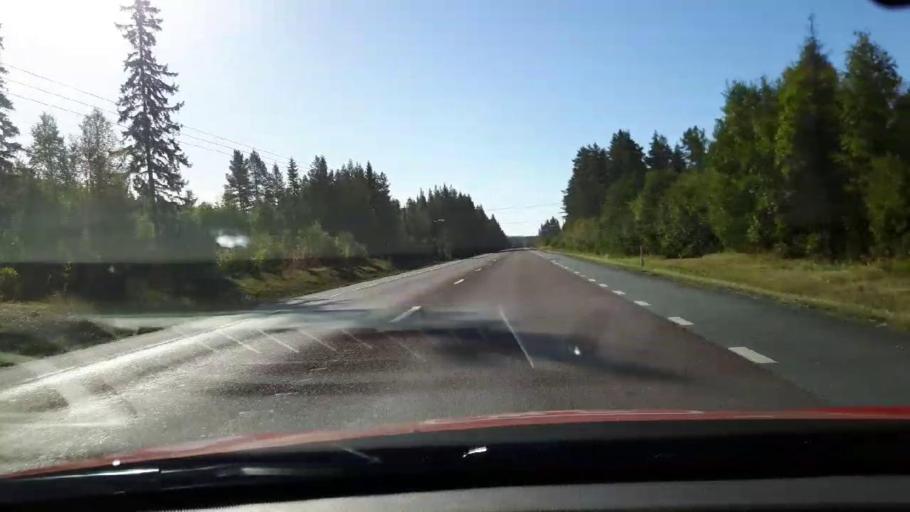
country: SE
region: Jaemtland
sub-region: Braecke Kommun
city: Braecke
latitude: 62.8626
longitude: 15.3127
